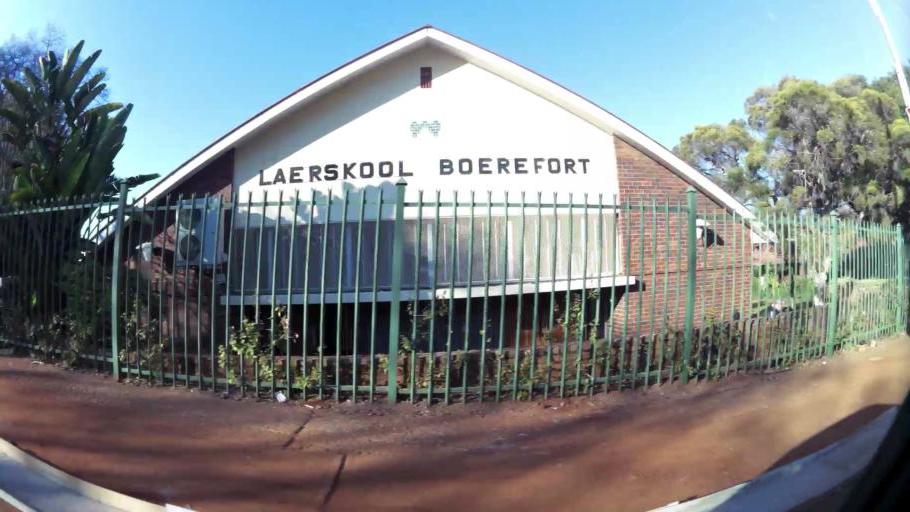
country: ZA
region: Gauteng
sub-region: City of Tshwane Metropolitan Municipality
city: Pretoria
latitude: -25.6999
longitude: 28.1923
